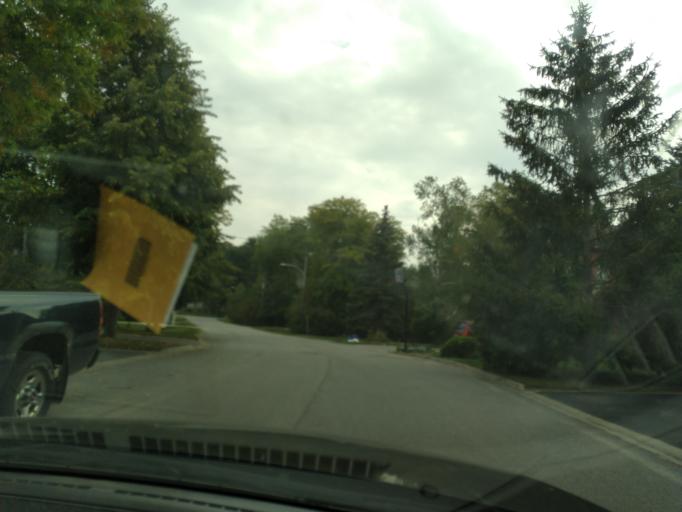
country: CA
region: Ontario
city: Keswick
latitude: 44.2478
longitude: -79.4786
